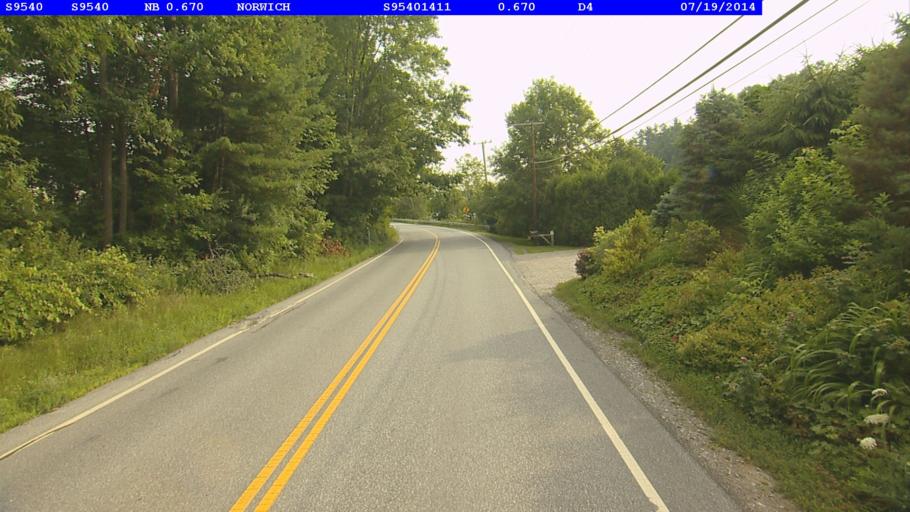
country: US
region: New Hampshire
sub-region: Grafton County
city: Hanover
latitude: 43.7112
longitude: -72.2931
